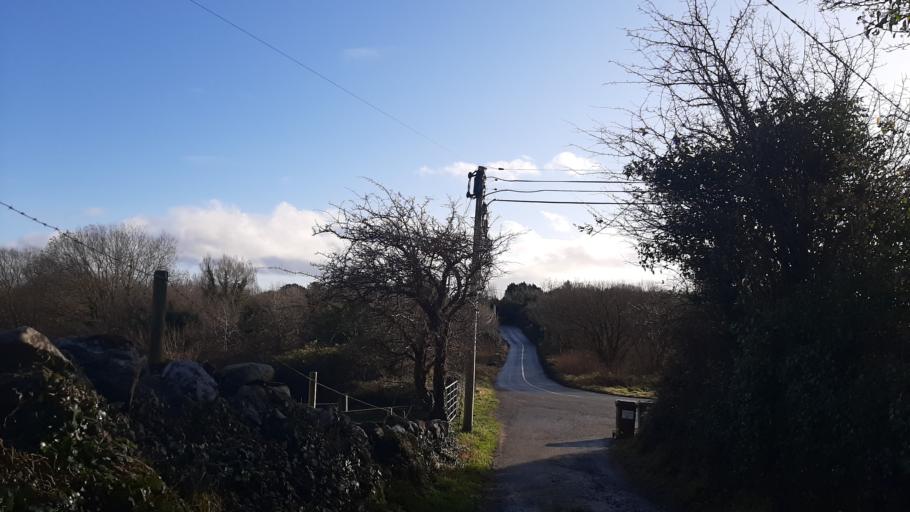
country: IE
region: Connaught
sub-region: County Galway
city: Gaillimh
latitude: 53.2998
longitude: -9.0569
